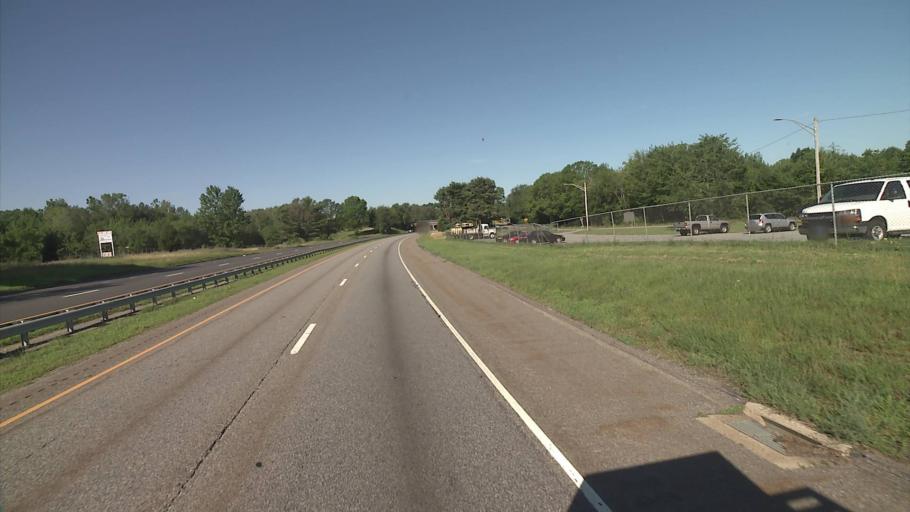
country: US
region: Connecticut
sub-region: New London County
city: Jewett City
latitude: 41.5925
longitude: -71.9721
